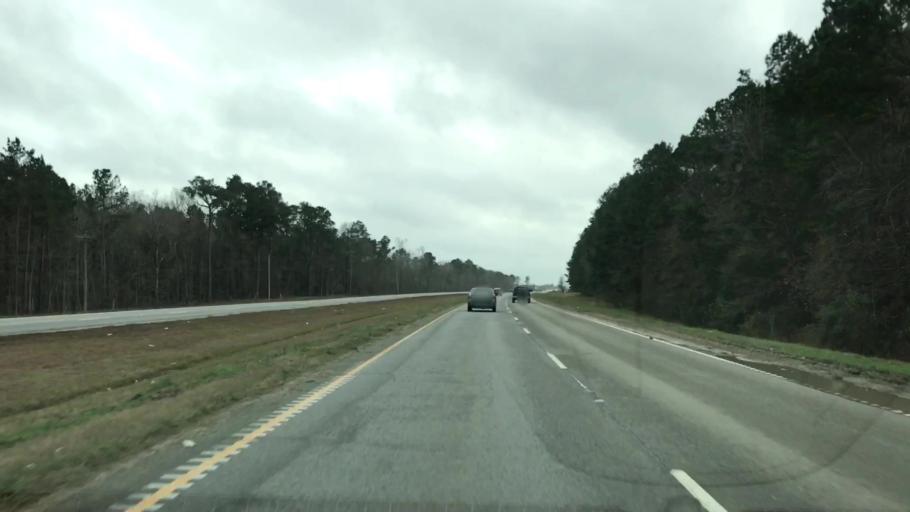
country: US
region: South Carolina
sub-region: Berkeley County
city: Moncks Corner
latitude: 33.1171
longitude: -80.0283
